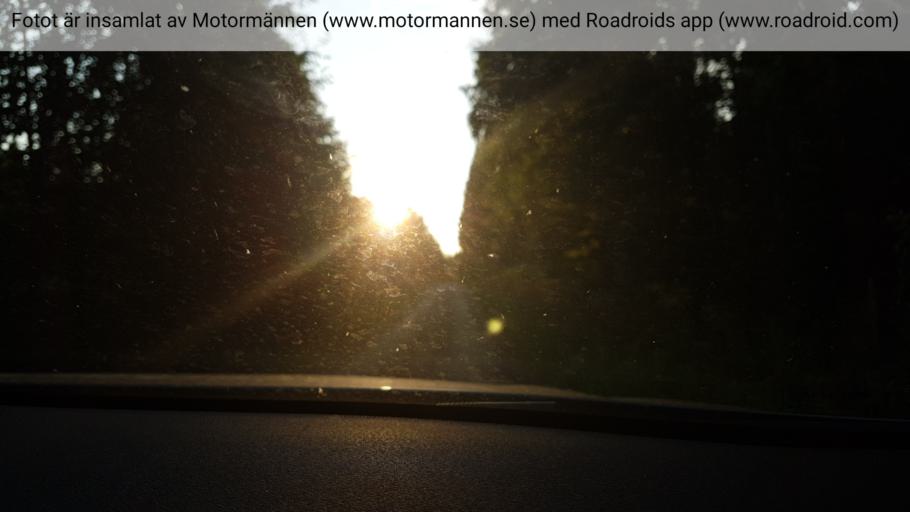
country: SE
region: Vaestra Goetaland
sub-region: Falkopings Kommun
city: Floby
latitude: 57.9750
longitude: 13.3560
